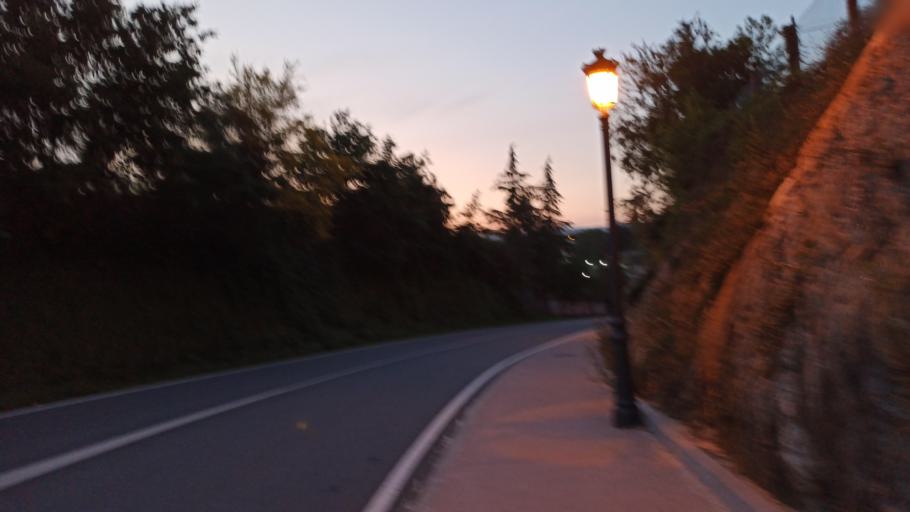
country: ES
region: Galicia
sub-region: Provincia da Coruna
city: Negreira
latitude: 42.9047
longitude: -8.7380
